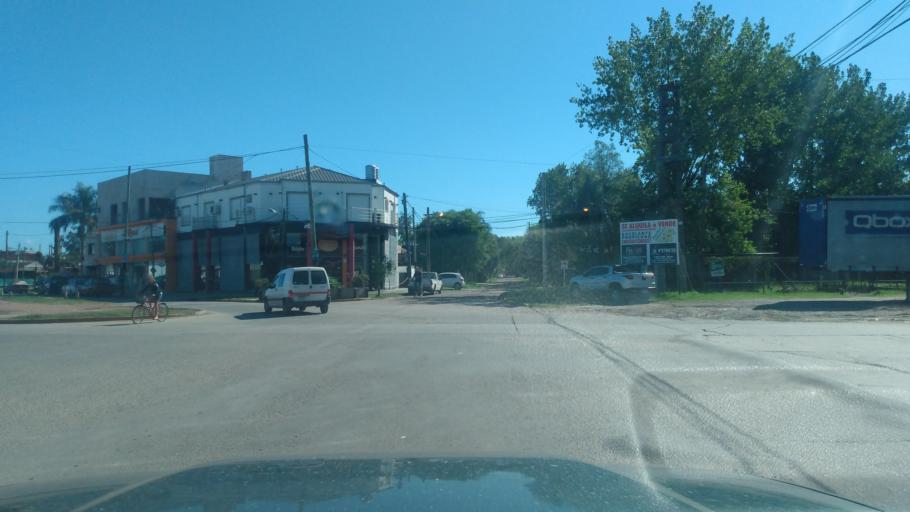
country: AR
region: Buenos Aires
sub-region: Partido de General Rodriguez
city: General Rodriguez
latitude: -34.5970
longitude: -58.9472
